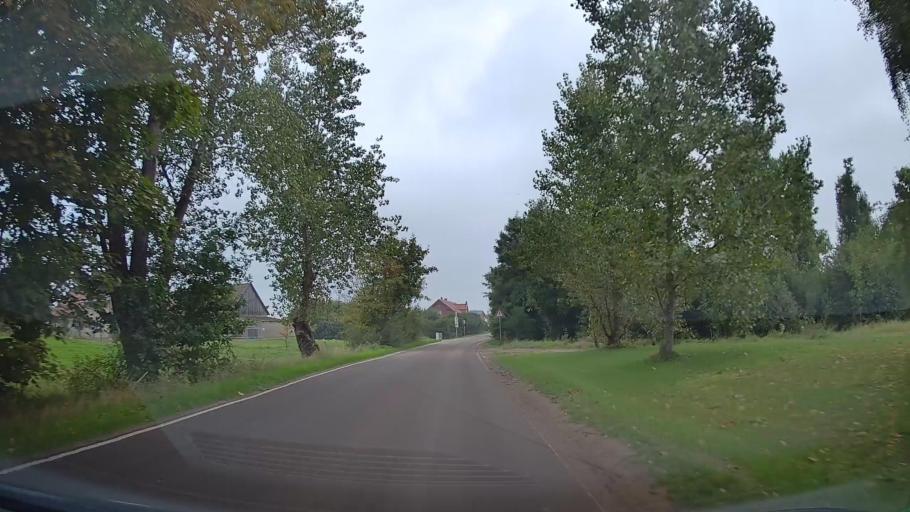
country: DE
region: Mecklenburg-Vorpommern
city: Blowatz
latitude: 53.9738
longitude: 11.5525
